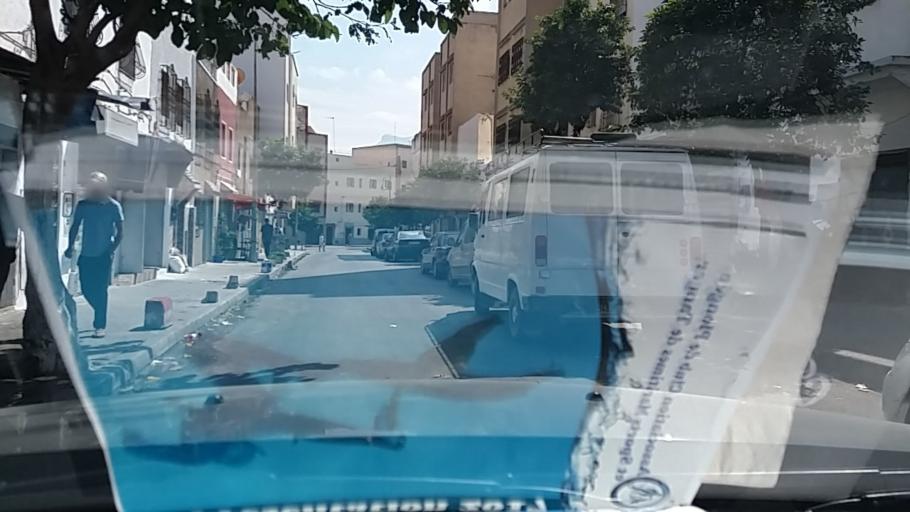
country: MA
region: Tanger-Tetouan
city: Tetouan
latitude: 35.5706
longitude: -5.3559
